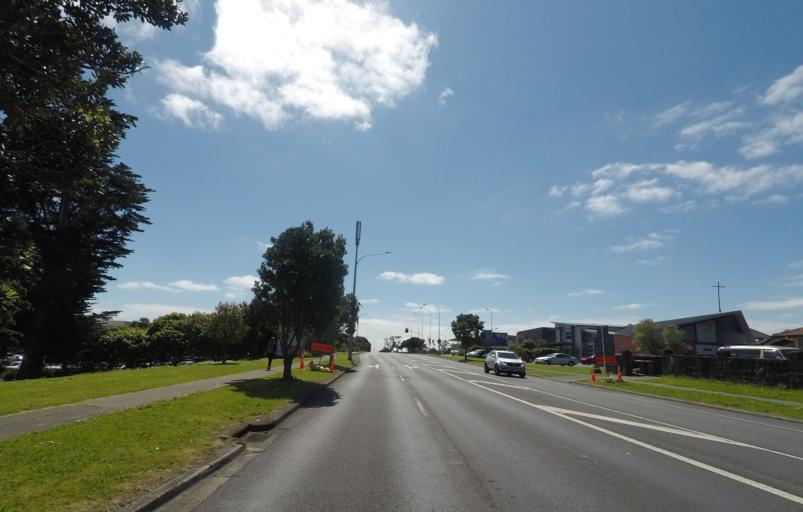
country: NZ
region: Auckland
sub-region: Auckland
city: Pakuranga
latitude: -36.9361
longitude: 174.9145
